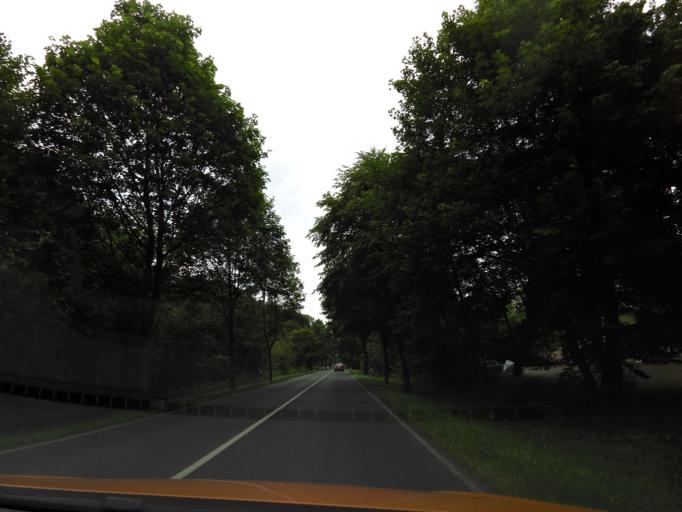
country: DE
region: Brandenburg
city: Zossen
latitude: 52.1920
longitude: 13.4614
